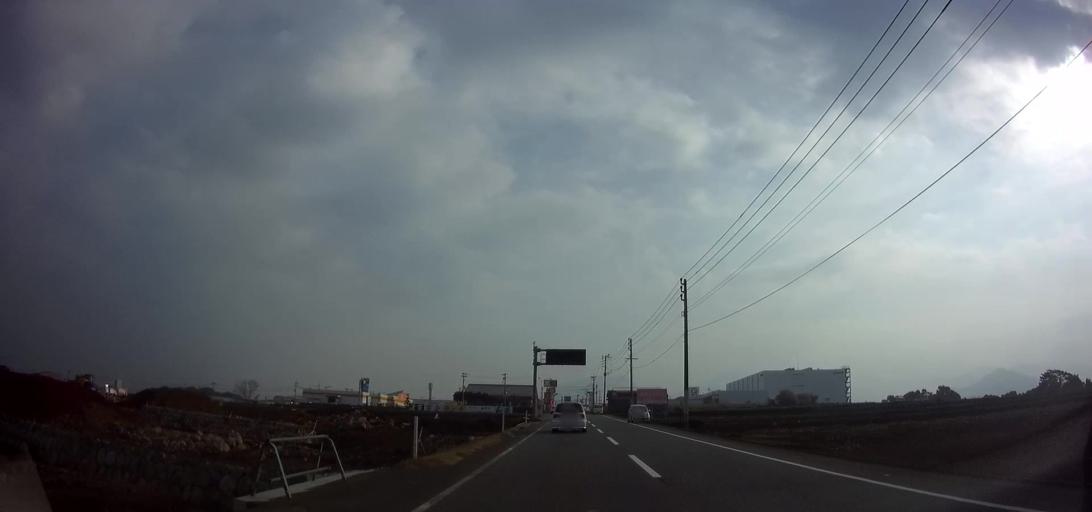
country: JP
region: Nagasaki
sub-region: Isahaya-shi
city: Isahaya
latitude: 32.7962
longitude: 130.1614
